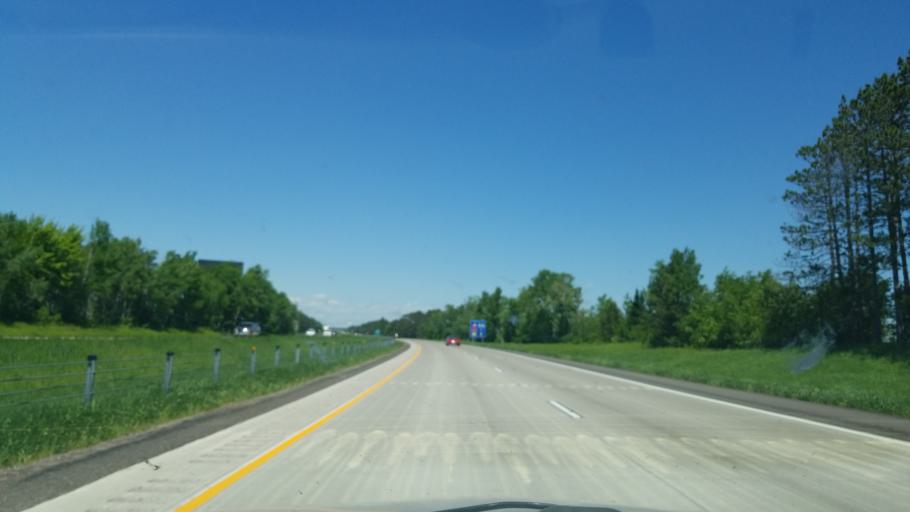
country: US
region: Minnesota
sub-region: Pine County
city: Hinckley
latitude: 45.9901
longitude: -92.9424
